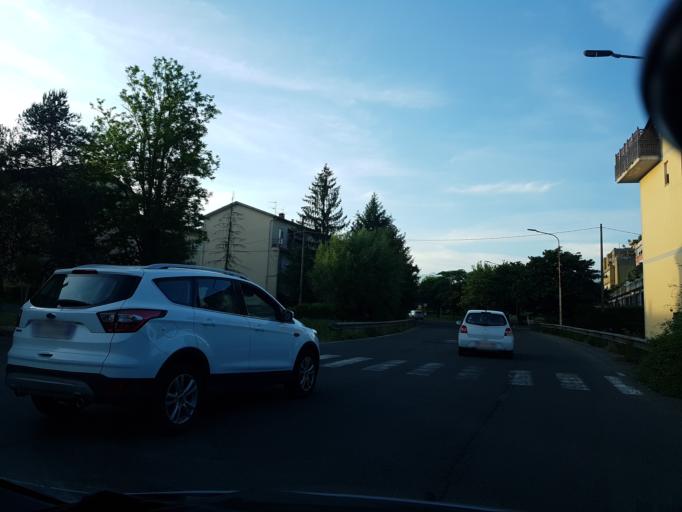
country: IT
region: Tuscany
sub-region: Provincia di Massa-Carrara
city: Aulla
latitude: 44.2182
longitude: 9.9699
